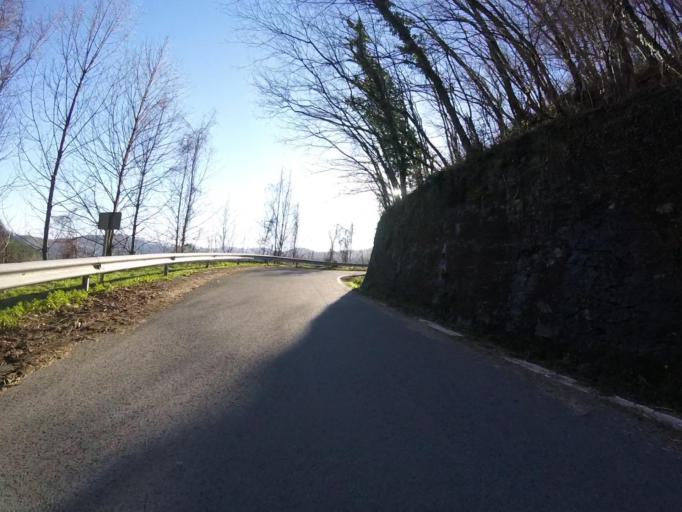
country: ES
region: Navarre
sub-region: Provincia de Navarra
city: Lesaka
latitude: 43.2648
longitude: -1.7390
